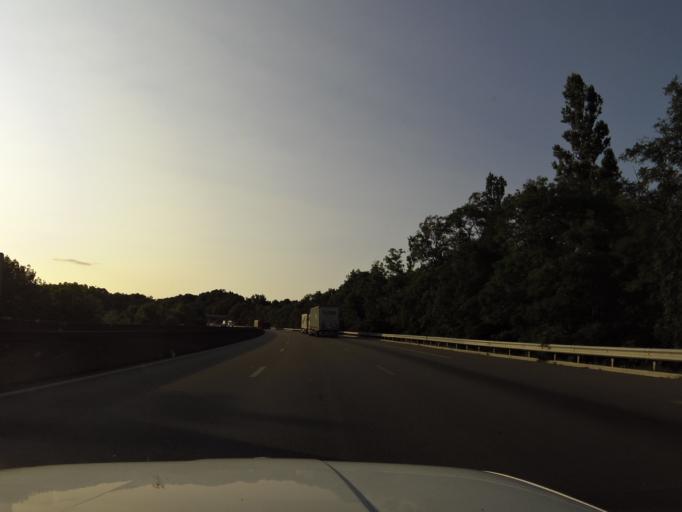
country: FR
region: Rhone-Alpes
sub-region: Departement de la Drome
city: Saint-Uze
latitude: 45.2038
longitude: 4.8767
